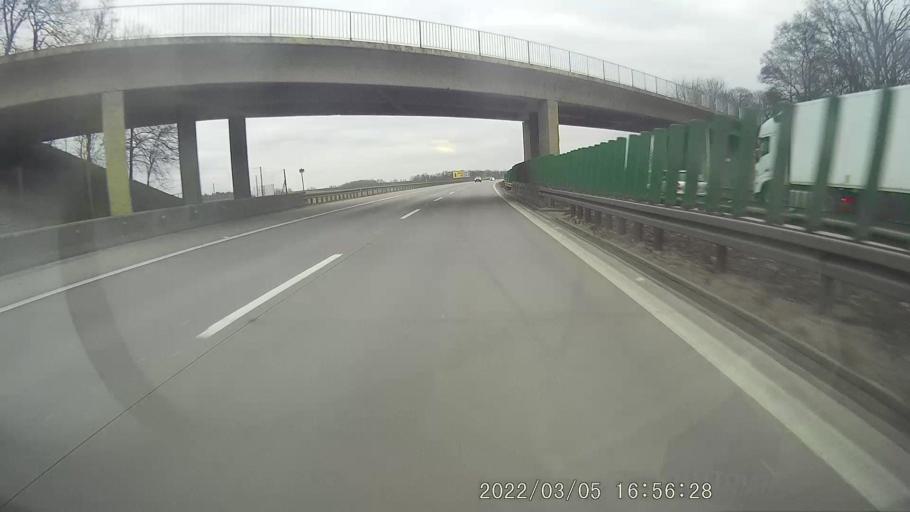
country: PL
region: Lower Silesian Voivodeship
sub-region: Powiat boleslawiecki
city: Nowogrodziec
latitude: 51.2667
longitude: 15.3728
